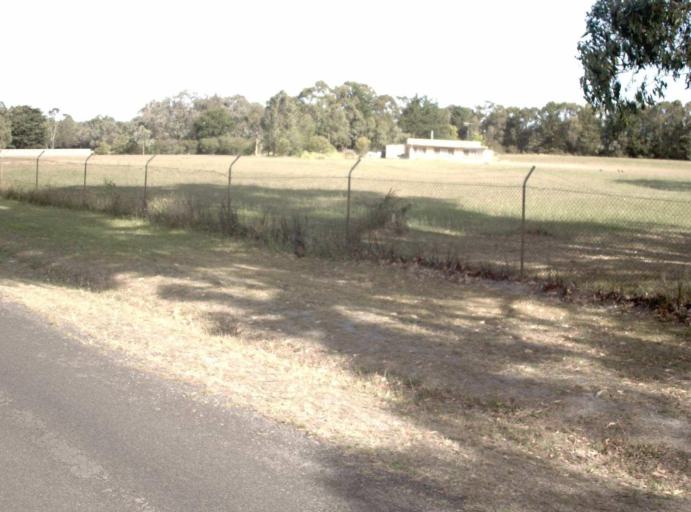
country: AU
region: Victoria
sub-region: Latrobe
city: Moe
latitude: -38.1703
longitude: 146.2875
